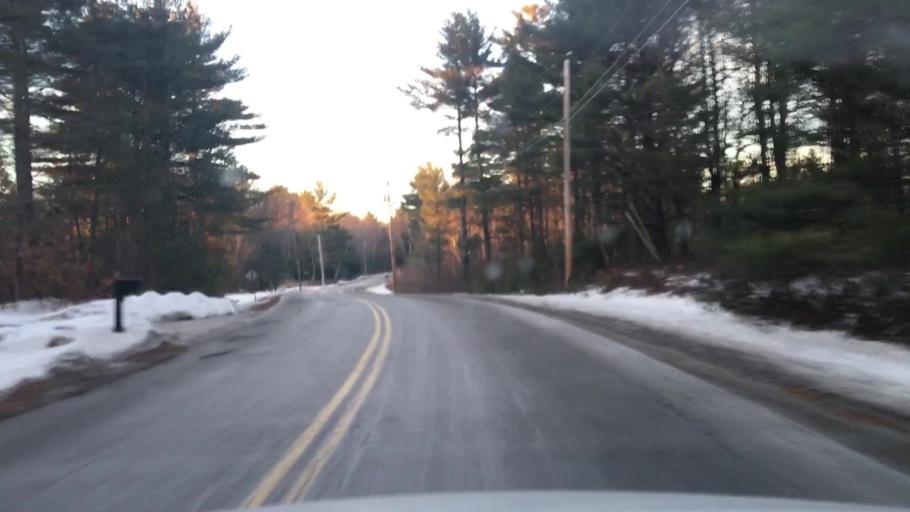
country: US
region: Maine
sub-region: York County
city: Lebanon
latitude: 43.3432
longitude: -70.8647
